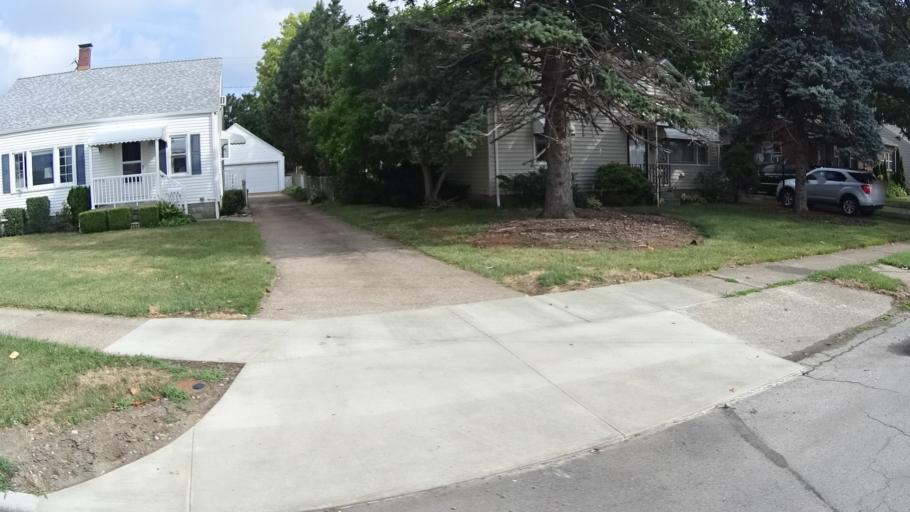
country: US
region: Ohio
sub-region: Erie County
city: Sandusky
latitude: 41.4328
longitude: -82.6959
